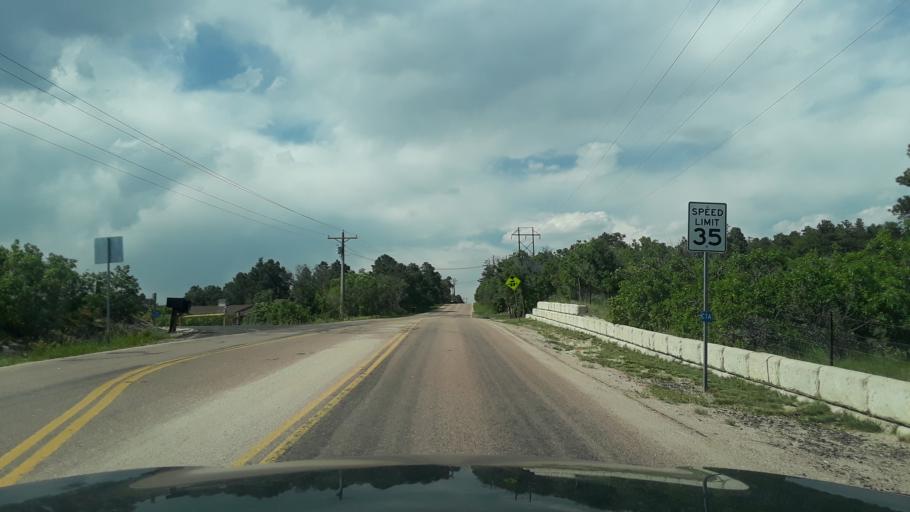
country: US
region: Colorado
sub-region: El Paso County
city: Gleneagle
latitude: 39.0353
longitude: -104.7847
